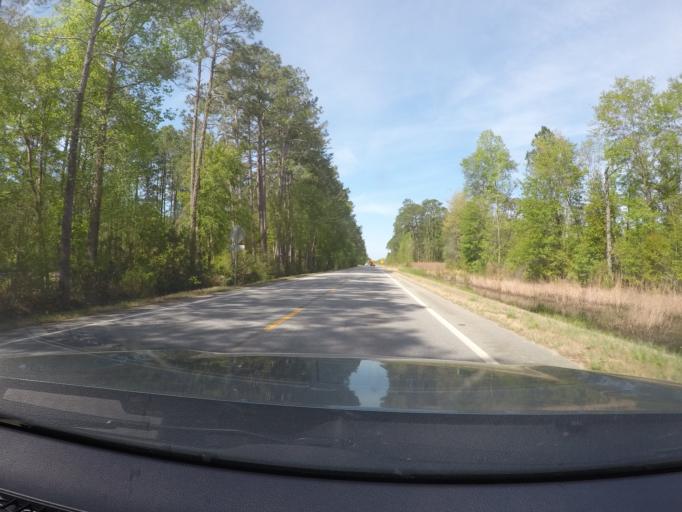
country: US
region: Georgia
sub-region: Bryan County
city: Pembroke
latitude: 32.1319
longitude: -81.5671
